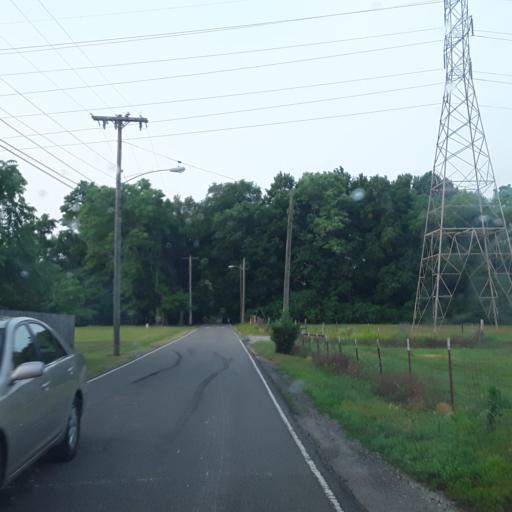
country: US
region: Tennessee
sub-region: Williamson County
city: Brentwood
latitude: 36.0548
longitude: -86.7632
